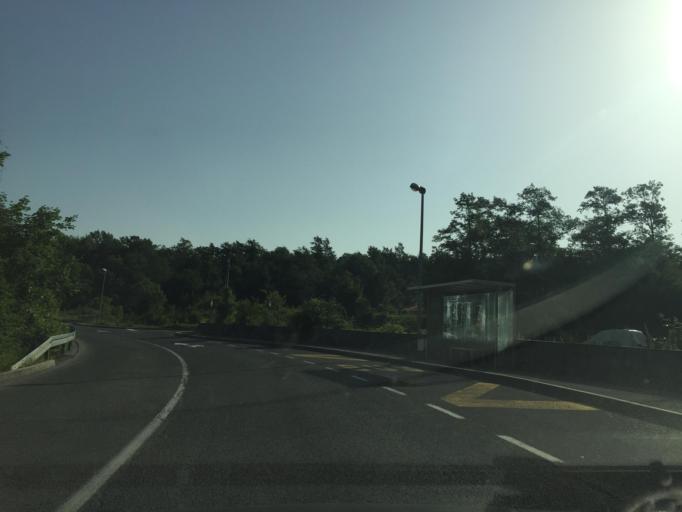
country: HR
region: Primorsko-Goranska
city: Matulji
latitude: 45.4104
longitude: 14.2911
